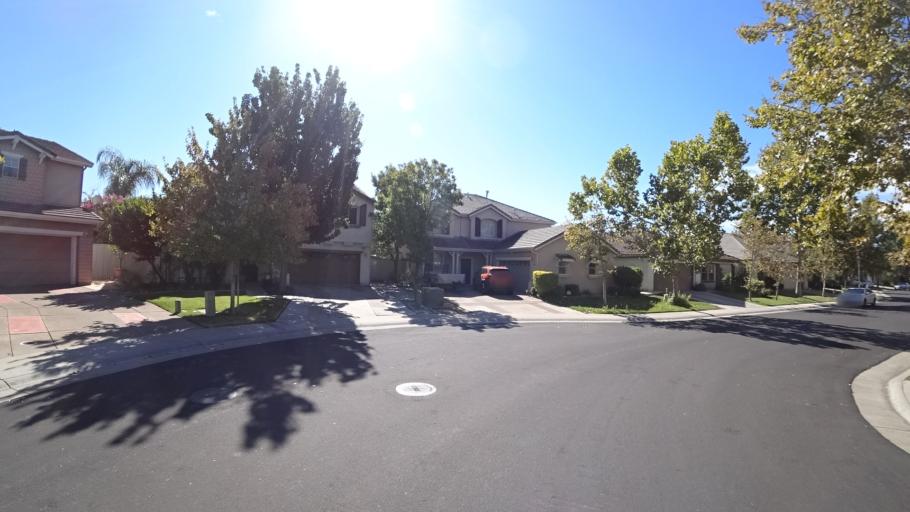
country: US
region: California
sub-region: Sacramento County
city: Laguna
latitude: 38.4223
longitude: -121.4733
